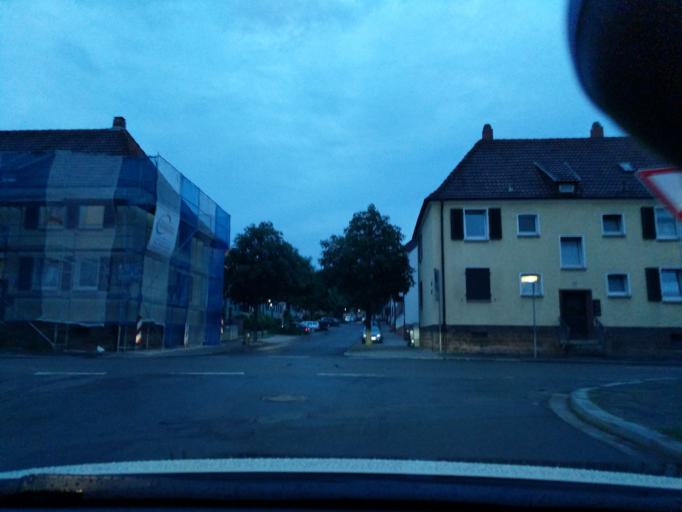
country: DE
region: Rheinland-Pfalz
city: Kaiserslautern
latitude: 49.4418
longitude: 7.7523
